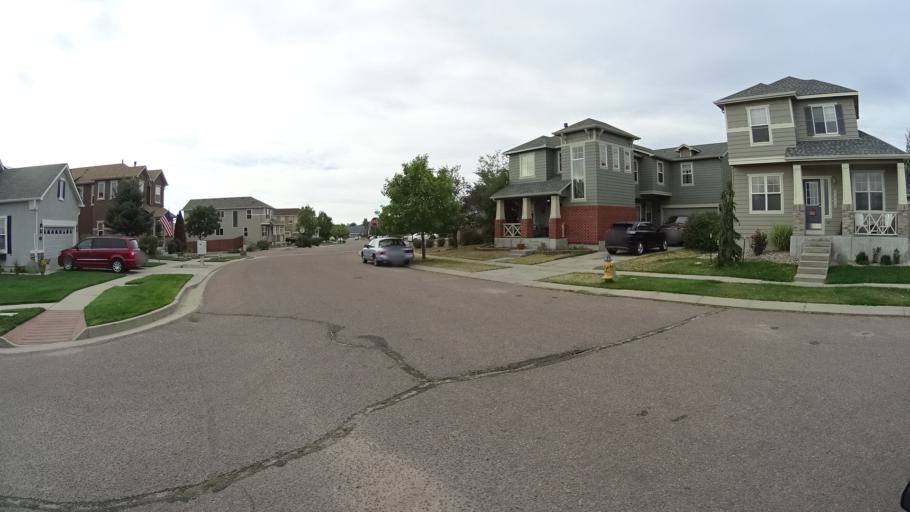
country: US
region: Colorado
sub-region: El Paso County
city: Cimarron Hills
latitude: 38.9206
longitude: -104.7030
